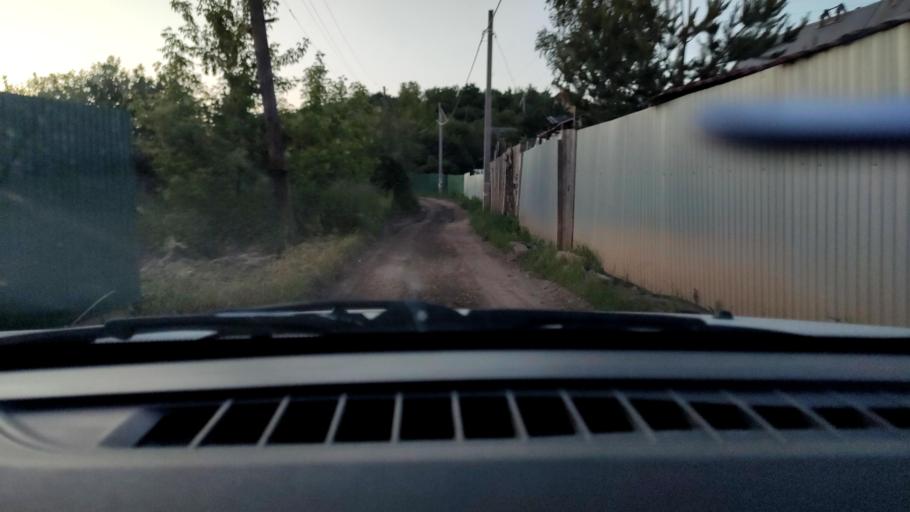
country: RU
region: Perm
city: Kondratovo
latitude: 57.9537
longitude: 56.1457
